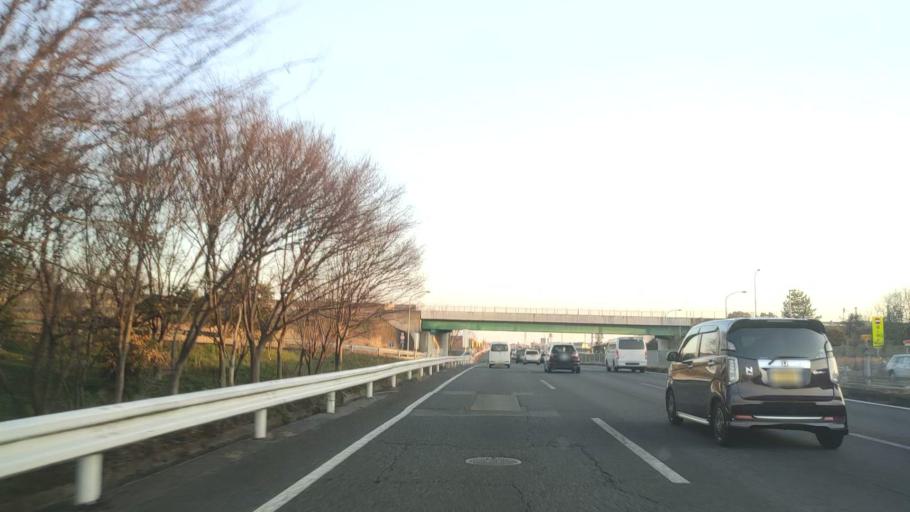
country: JP
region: Aichi
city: Kuroda
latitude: 35.3417
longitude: 136.7971
